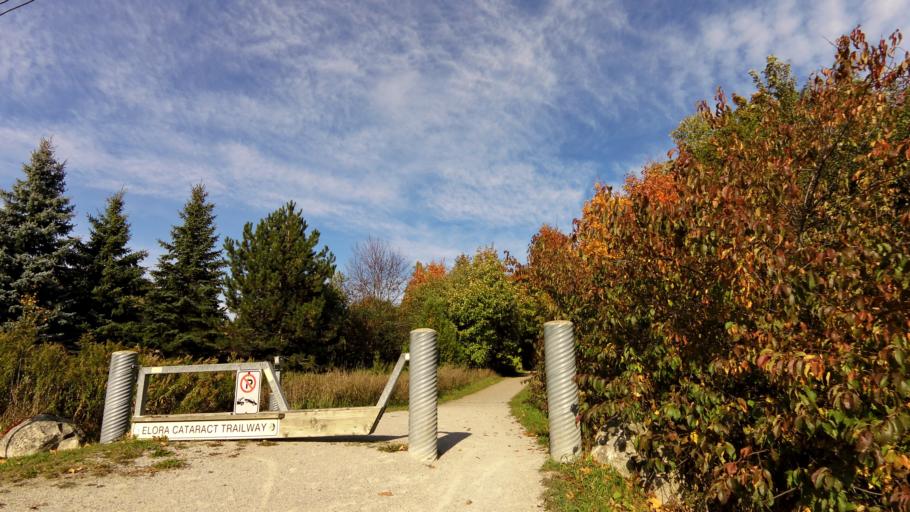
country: CA
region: Ontario
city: Orangeville
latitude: 43.7841
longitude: -80.0586
